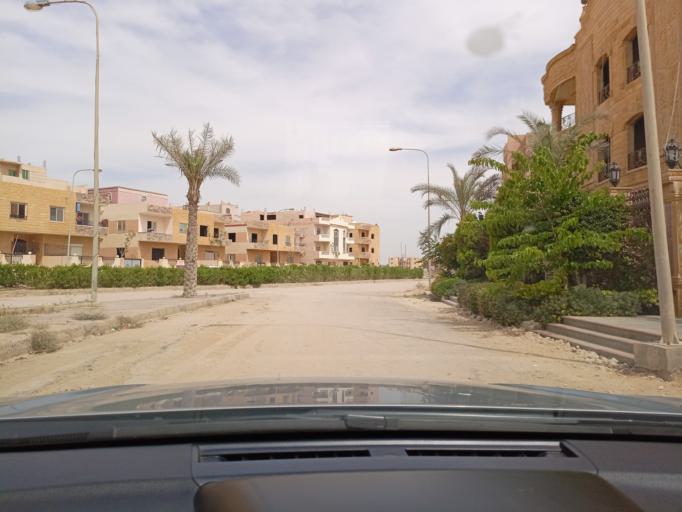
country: EG
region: Muhafazat al Qalyubiyah
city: Al Khankah
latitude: 30.2478
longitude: 31.5027
